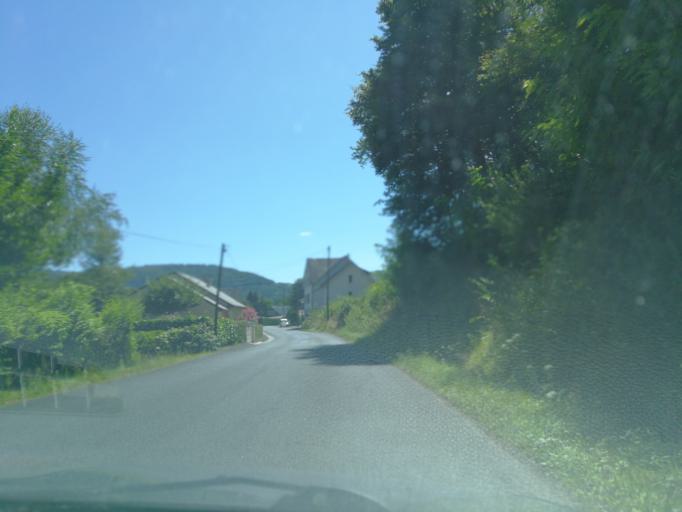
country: FR
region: Limousin
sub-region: Departement de la Correze
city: Argentat
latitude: 45.0951
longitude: 1.9210
